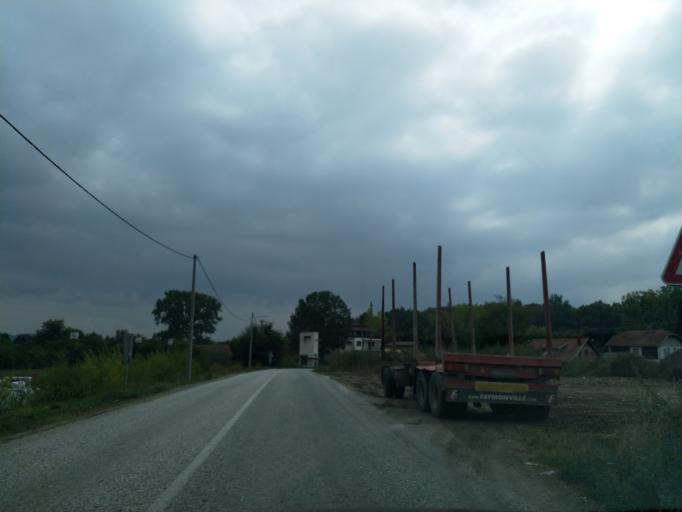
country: RS
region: Central Serbia
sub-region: Sumadijski Okrug
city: Batocina
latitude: 44.1501
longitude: 21.1058
